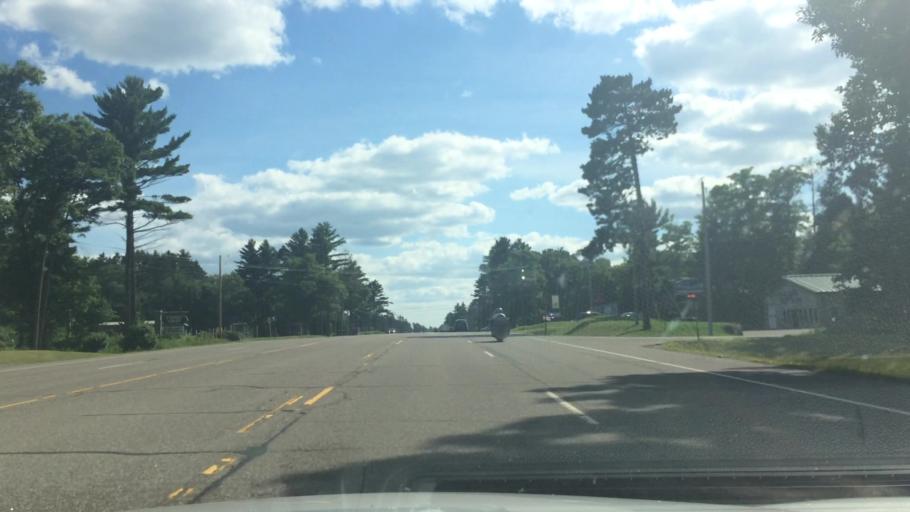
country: US
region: Wisconsin
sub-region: Vilas County
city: Lac du Flambeau
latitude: 45.8348
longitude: -89.7123
